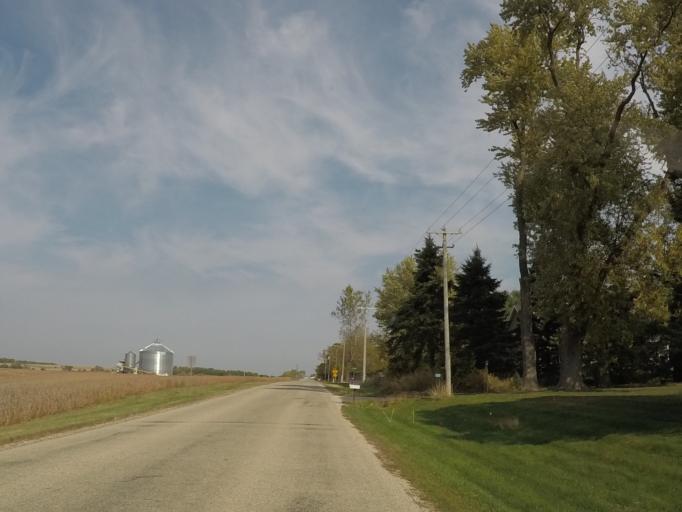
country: US
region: Wisconsin
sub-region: Dane County
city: Cross Plains
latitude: 43.0562
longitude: -89.6009
